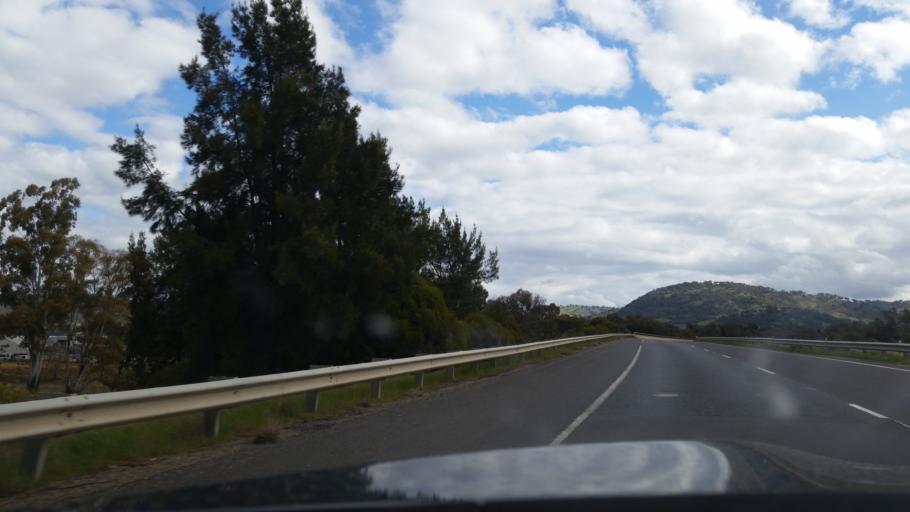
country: AU
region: Victoria
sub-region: Wodonga
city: Wodonga
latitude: -36.1079
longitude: 146.8635
